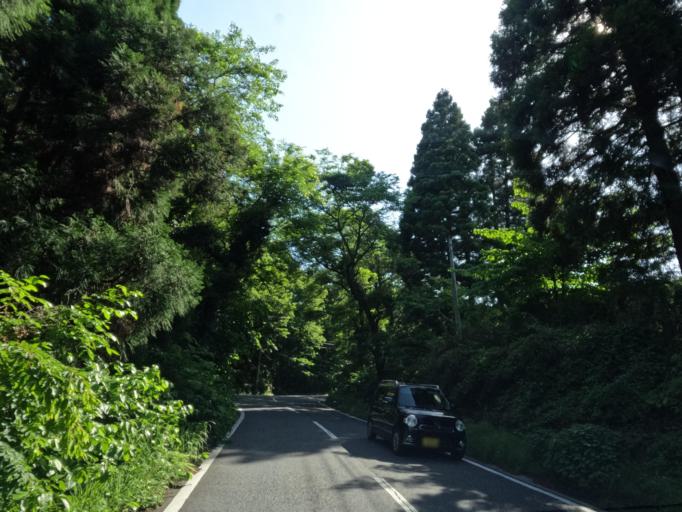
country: JP
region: Saitama
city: Yorii
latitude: 36.0482
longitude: 139.1601
